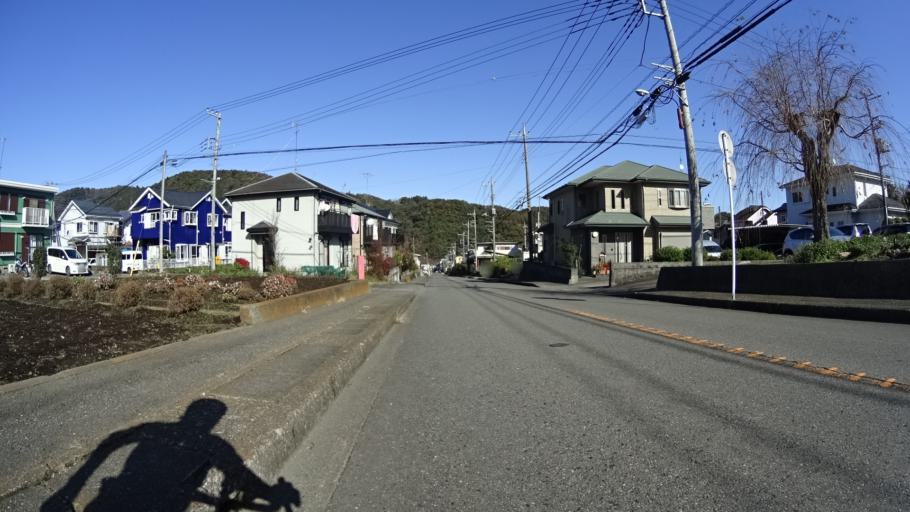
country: JP
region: Kanagawa
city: Zama
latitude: 35.5365
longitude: 139.2728
